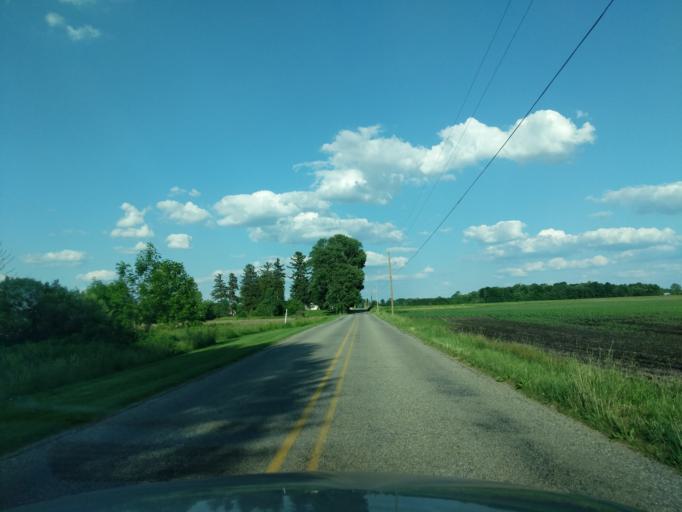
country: US
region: Indiana
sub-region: Whitley County
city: Tri-Lakes
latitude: 41.3024
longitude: -85.5287
